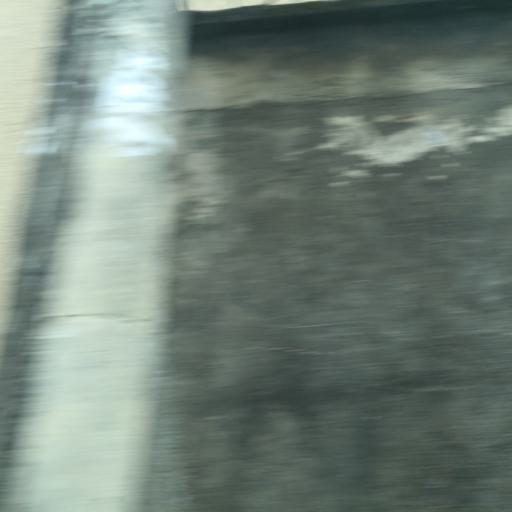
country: NG
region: Rivers
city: Port Harcourt
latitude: 4.8282
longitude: 7.0402
